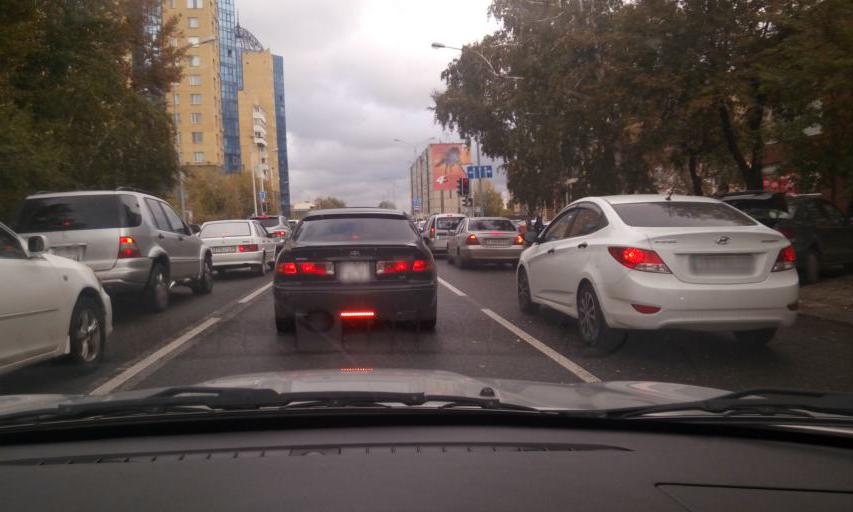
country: KZ
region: Astana Qalasy
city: Astana
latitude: 51.1697
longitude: 71.4381
